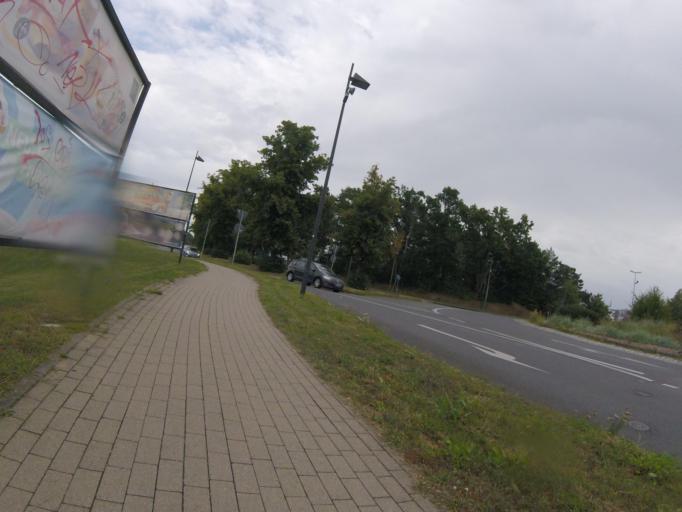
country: DE
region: Brandenburg
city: Wildau
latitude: 52.3170
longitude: 13.6028
